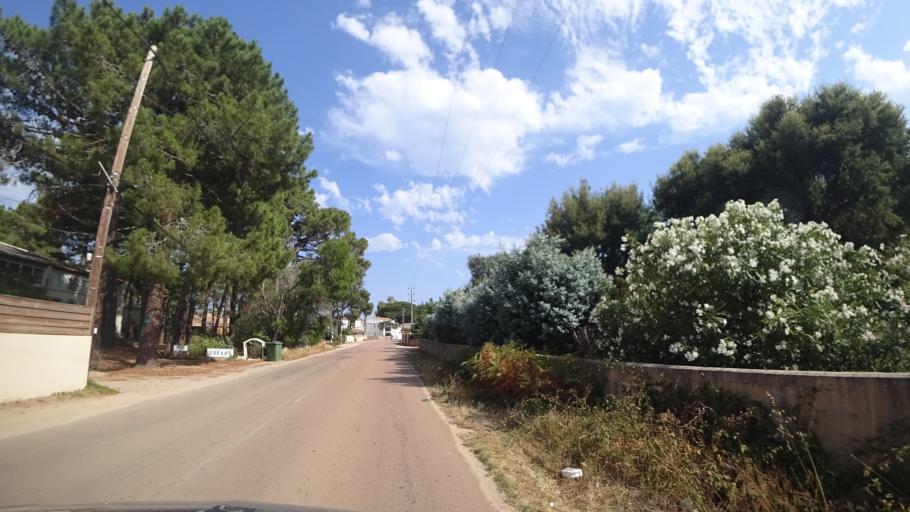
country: FR
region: Corsica
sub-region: Departement de la Corse-du-Sud
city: Porto-Vecchio
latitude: 41.6301
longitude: 9.3332
